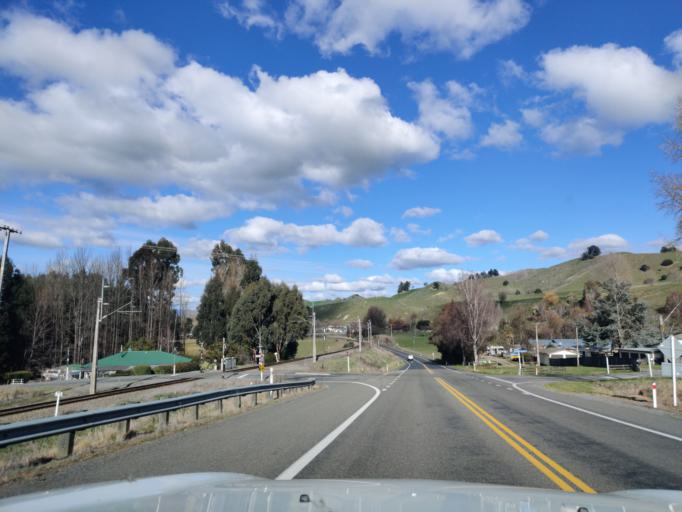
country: NZ
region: Manawatu-Wanganui
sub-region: Ruapehu District
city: Waiouru
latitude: -39.6866
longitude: 175.8073
